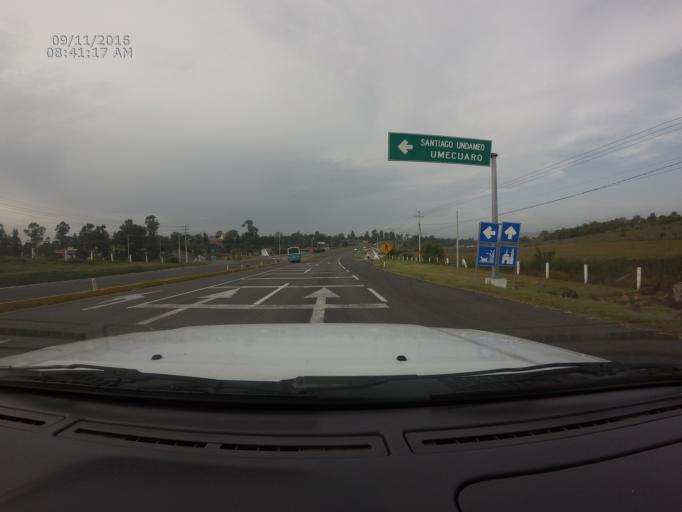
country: MX
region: Michoacan
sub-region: Morelia
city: La Mintzita (Piedra Dura)
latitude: 19.6005
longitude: -101.2906
